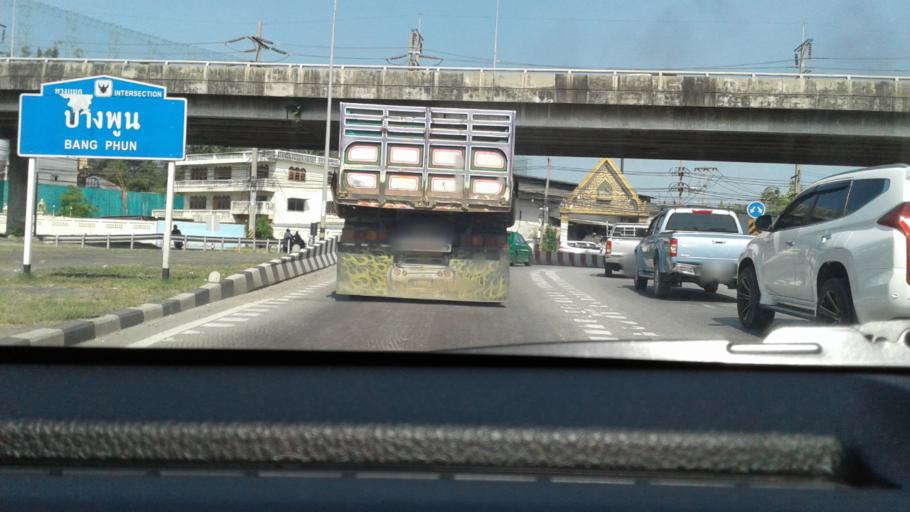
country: TH
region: Phra Nakhon Si Ayutthaya
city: Ban Bang Kadi Pathum Thani
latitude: 13.9840
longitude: 100.5926
